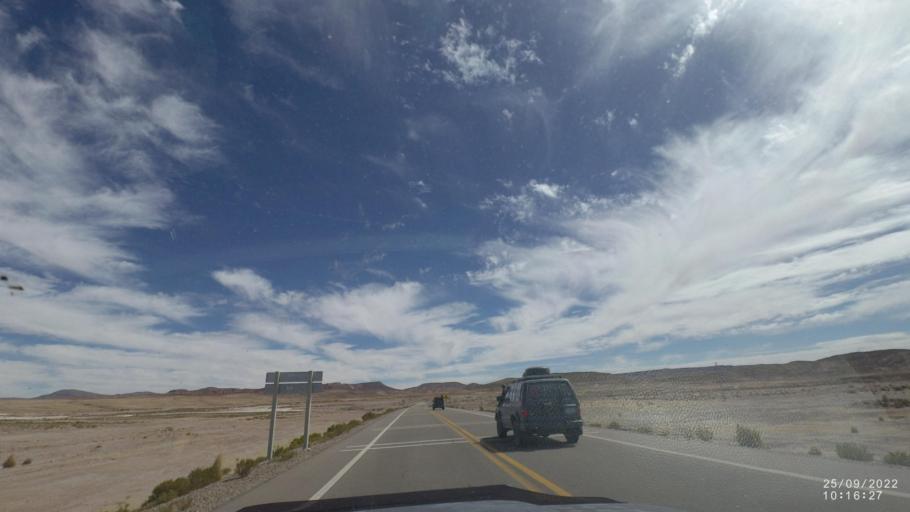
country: BO
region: Potosi
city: Colchani
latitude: -20.0302
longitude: -66.8697
